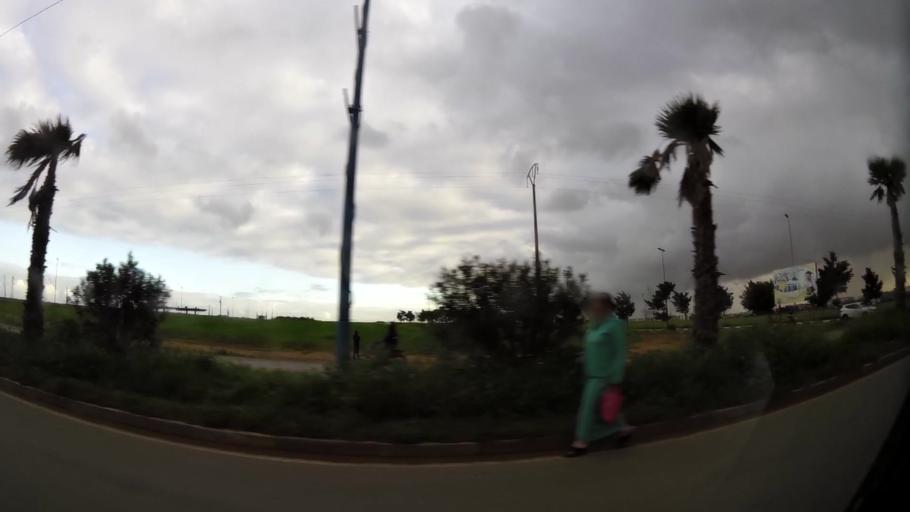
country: MA
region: Grand Casablanca
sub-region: Mediouna
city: Tit Mellil
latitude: 33.5650
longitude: -7.4994
